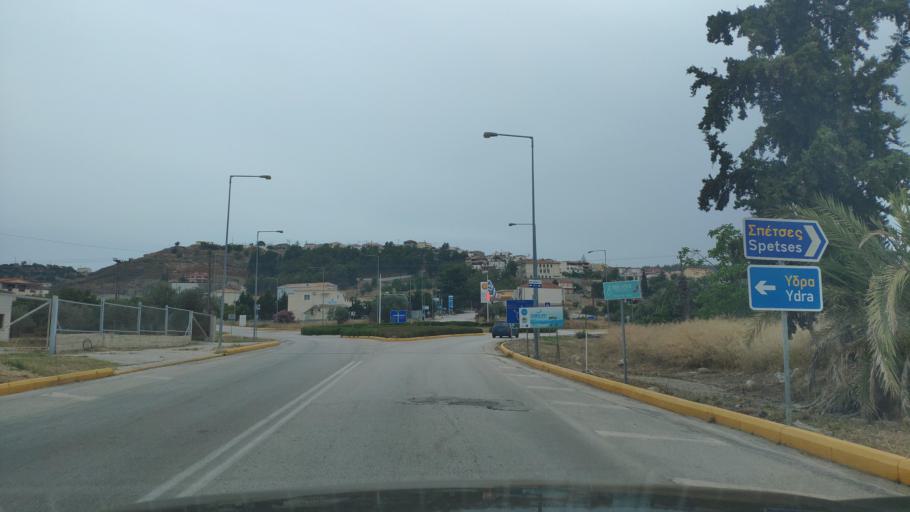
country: GR
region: Peloponnese
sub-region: Nomos Argolidos
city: Kranidi
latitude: 37.3882
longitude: 23.1583
